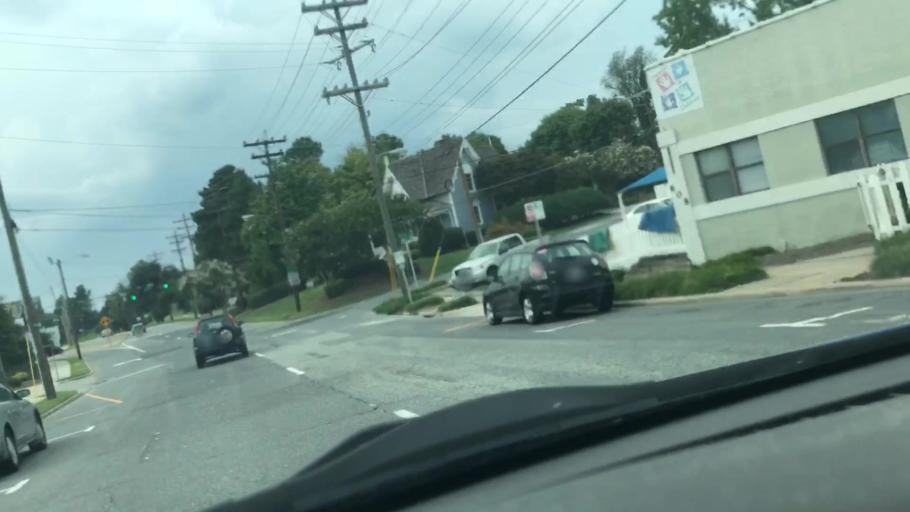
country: US
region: North Carolina
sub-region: Guilford County
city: Greensboro
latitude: 36.0793
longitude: -79.7943
